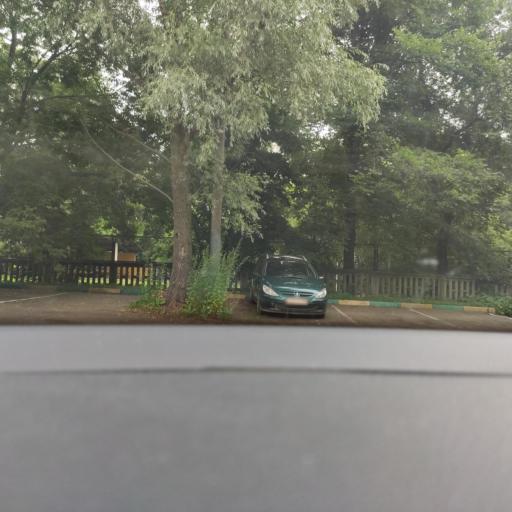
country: RU
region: Moscow
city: Gol'yanovo
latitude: 55.8216
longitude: 37.8153
